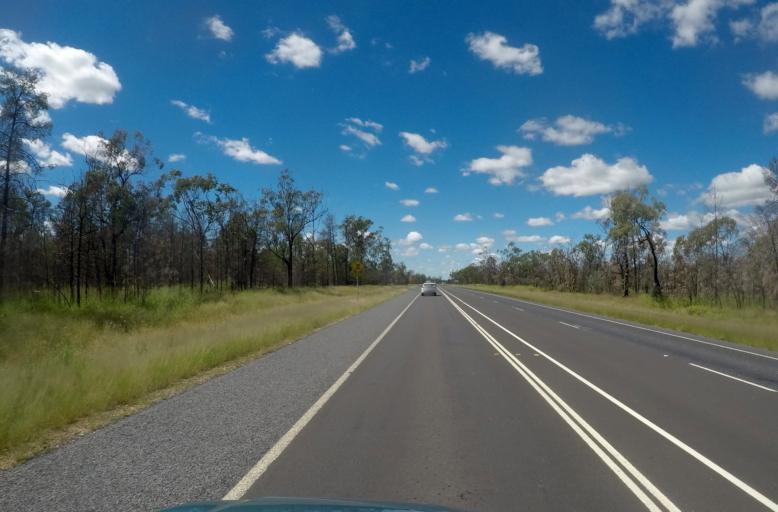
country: AU
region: Queensland
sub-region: Western Downs
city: Westcourt
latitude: -26.6706
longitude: 150.3272
